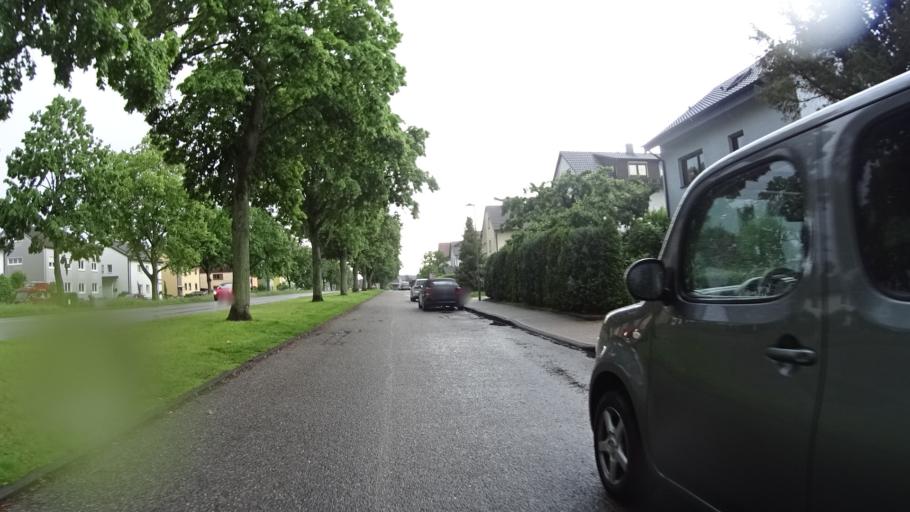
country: DE
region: Baden-Wuerttemberg
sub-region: Karlsruhe Region
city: Durmersheim
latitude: 48.9417
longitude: 8.2771
